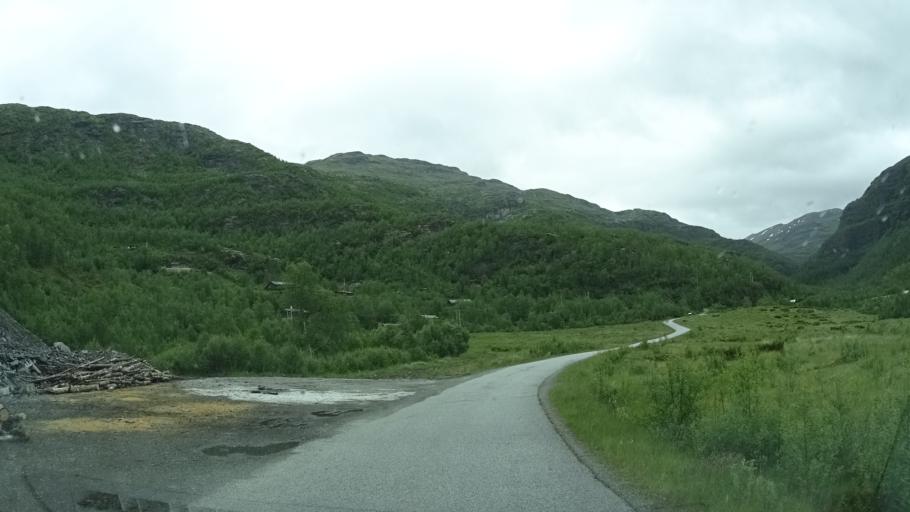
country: NO
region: Sogn og Fjordane
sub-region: Laerdal
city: Laerdalsoyri
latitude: 60.8275
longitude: 7.5120
